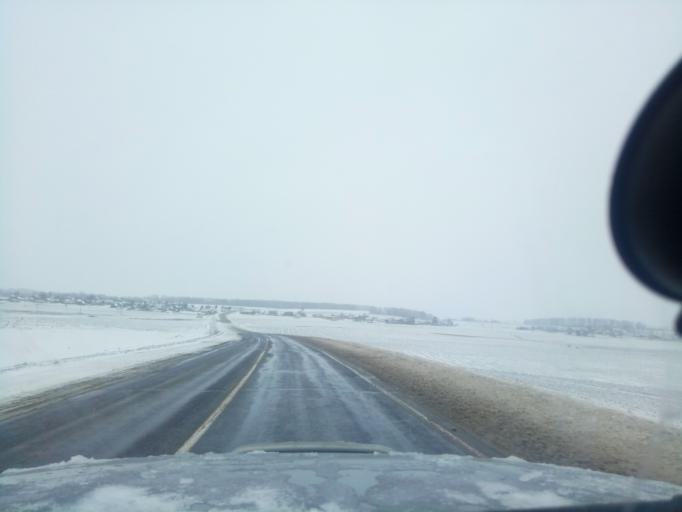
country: BY
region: Minsk
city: Haradzyeya
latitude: 53.3327
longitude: 26.5289
